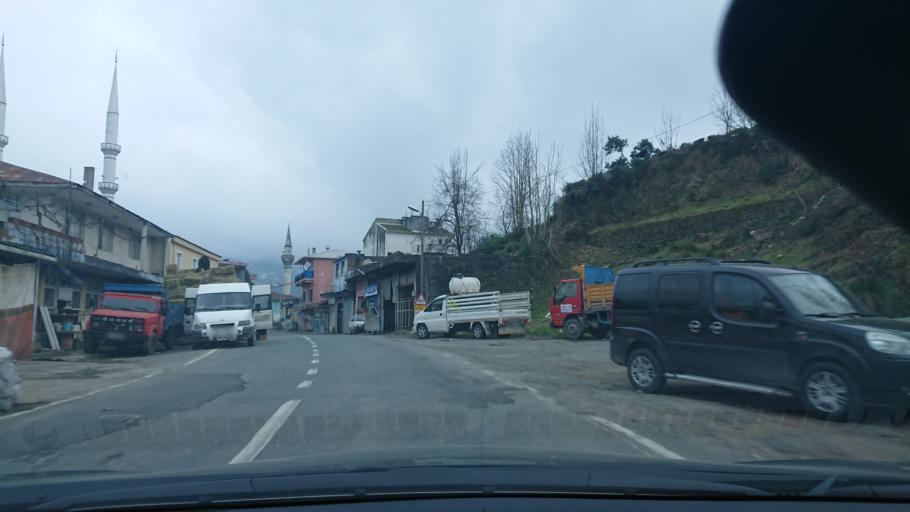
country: TR
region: Rize
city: Rize
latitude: 41.0002
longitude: 40.4875
